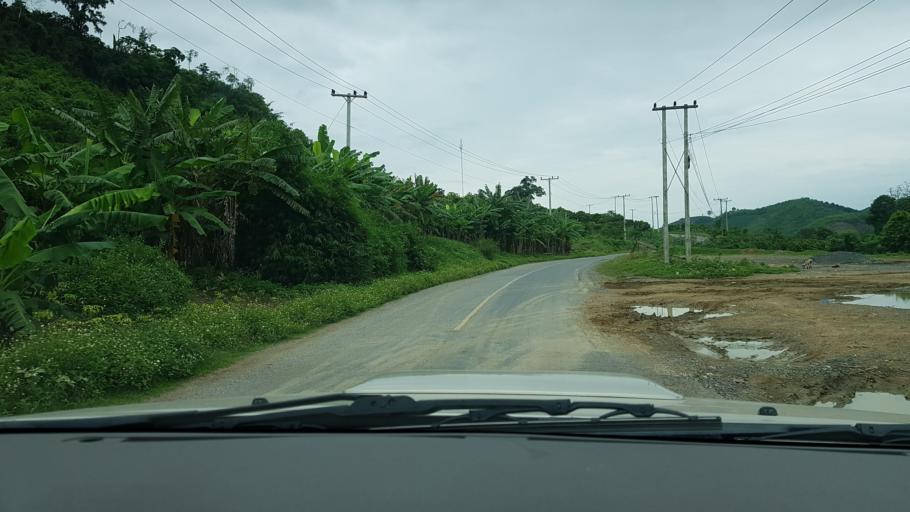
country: LA
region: Loungnamtha
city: Muang Nale
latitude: 20.1765
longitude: 101.5155
